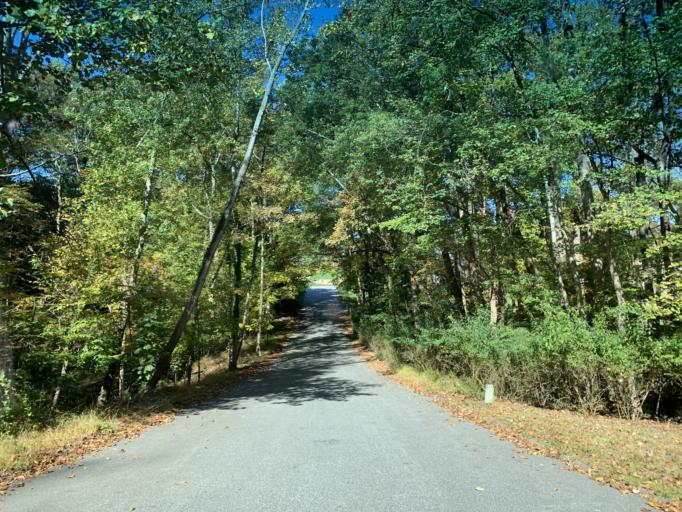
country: US
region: Maryland
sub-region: Harford County
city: Bel Air South
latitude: 39.5196
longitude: -76.3229
